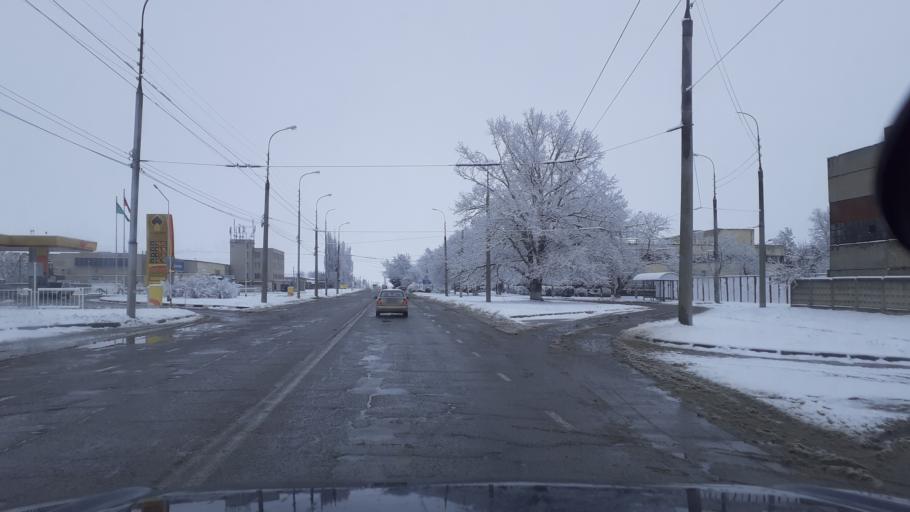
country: RU
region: Adygeya
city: Maykop
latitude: 44.6311
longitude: 40.1240
